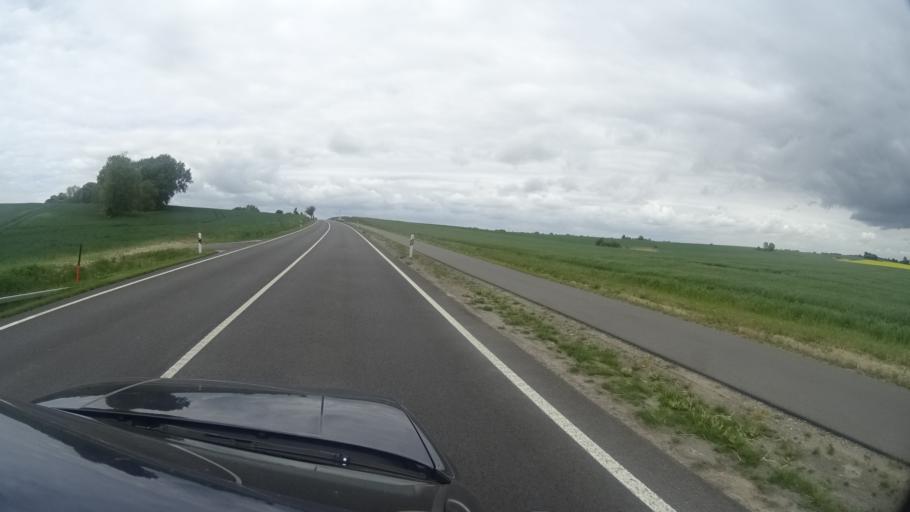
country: DE
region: Brandenburg
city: Fehrbellin
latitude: 52.8532
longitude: 12.7778
